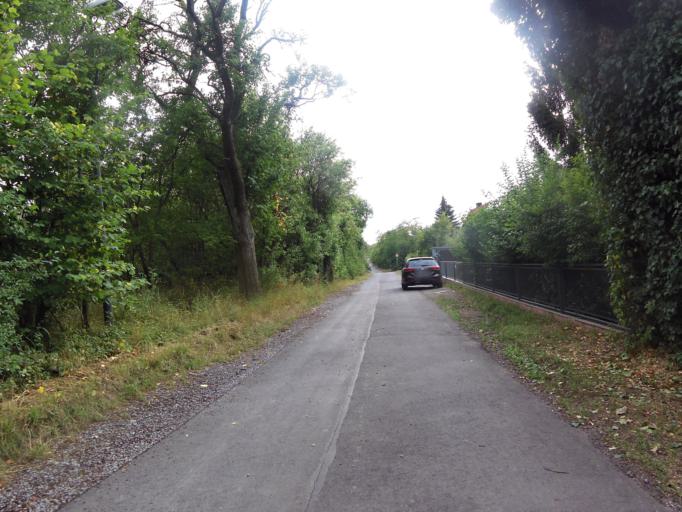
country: DE
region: Bavaria
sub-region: Regierungsbezirk Unterfranken
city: Hochberg
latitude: 49.7795
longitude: 9.8839
